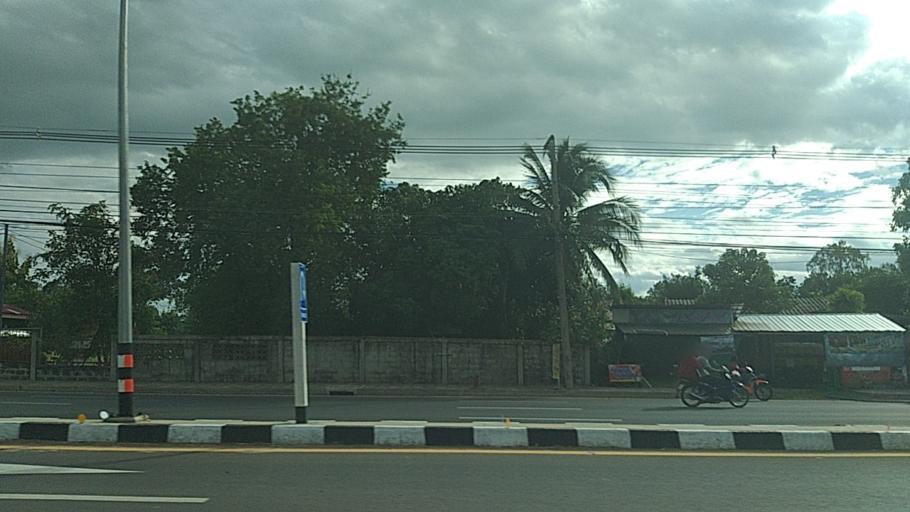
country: TH
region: Surin
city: Prasat
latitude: 14.6137
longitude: 103.4173
